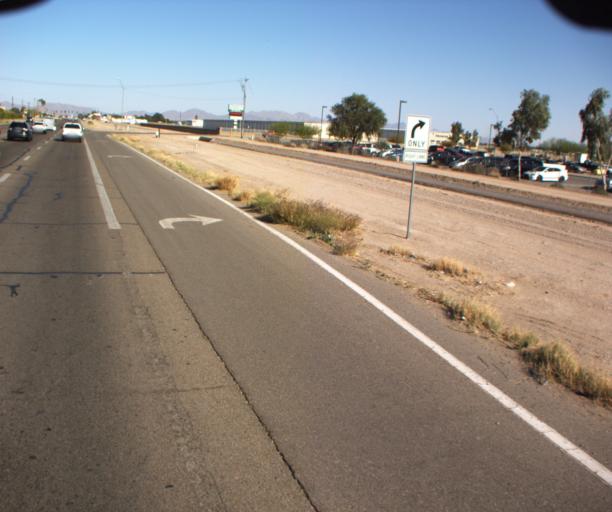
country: US
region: Arizona
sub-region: Yuma County
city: Yuma
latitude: 32.6697
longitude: -114.5699
